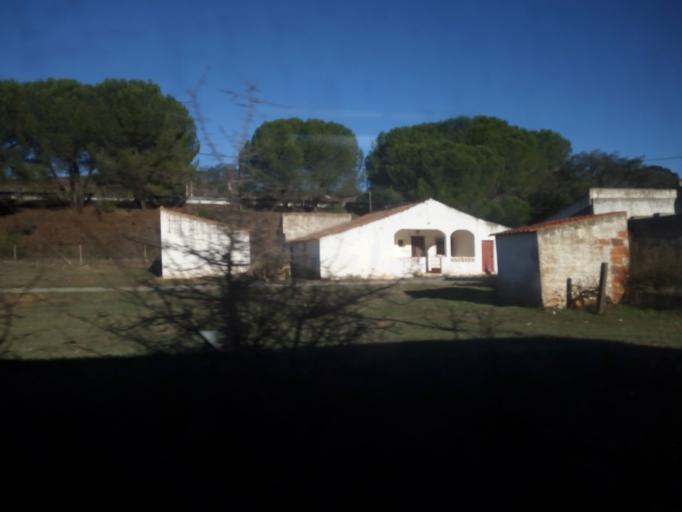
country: PT
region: Faro
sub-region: Silves
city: Sao Bartolomeu de Messines
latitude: 37.3419
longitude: -8.3556
